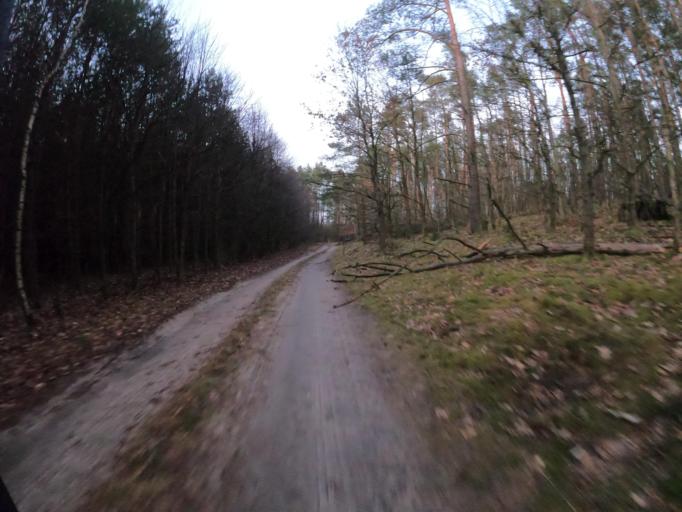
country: PL
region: Greater Poland Voivodeship
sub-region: Powiat zlotowski
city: Sypniewo
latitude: 53.4810
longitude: 16.6345
